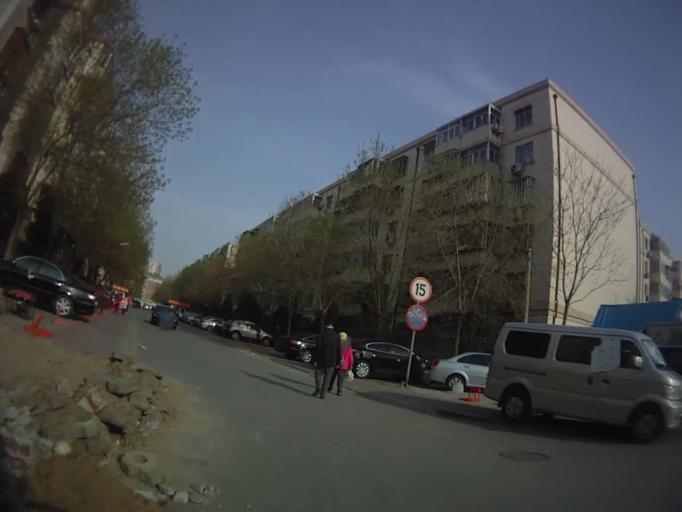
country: CN
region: Beijing
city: Longtan
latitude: 39.8981
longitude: 116.4417
